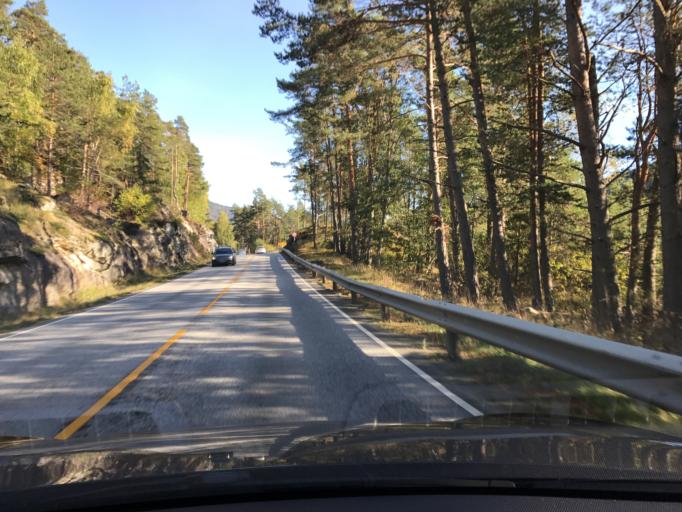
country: NO
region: Sogn og Fjordane
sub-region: Sogndal
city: Sogndalsfjora
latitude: 61.2070
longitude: 7.1629
